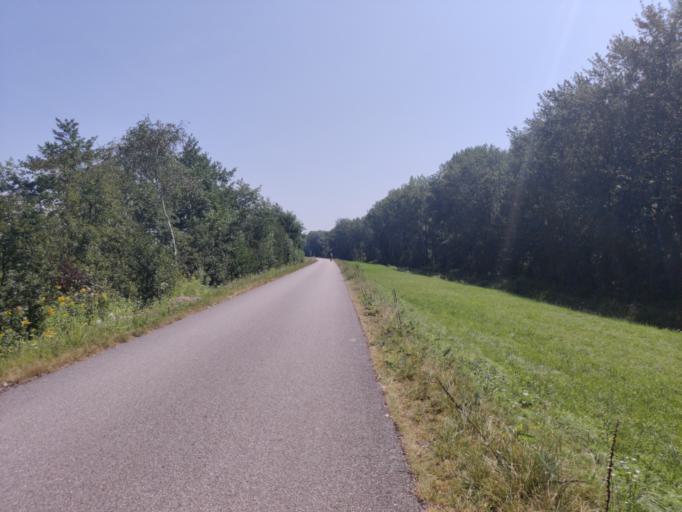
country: AT
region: Upper Austria
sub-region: Politischer Bezirk Urfahr-Umgebung
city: Feldkirchen an der Donau
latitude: 48.3174
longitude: 14.0670
